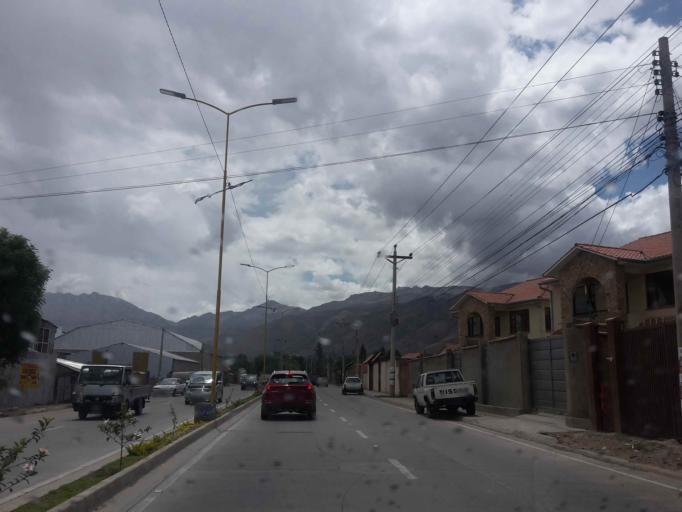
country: BO
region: Cochabamba
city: Cochabamba
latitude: -17.3430
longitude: -66.2026
